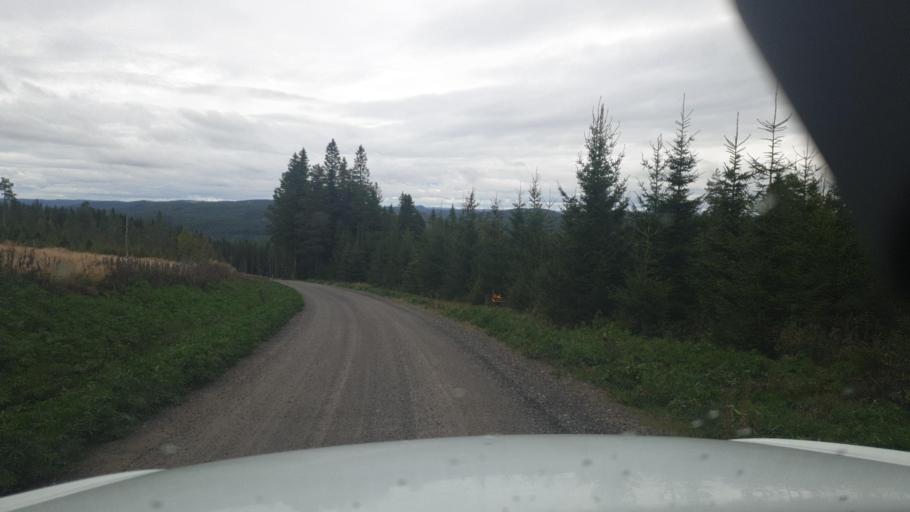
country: SE
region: Vaermland
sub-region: Torsby Kommun
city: Torsby
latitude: 60.1747
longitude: 12.6465
